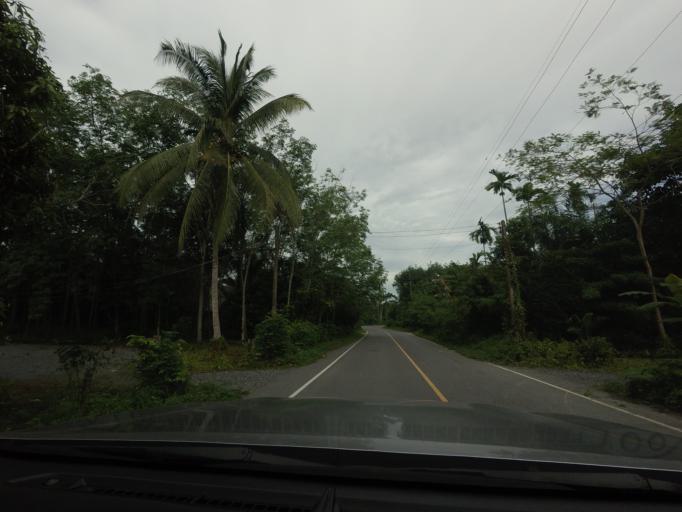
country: TH
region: Nakhon Si Thammarat
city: Phra Phrom
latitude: 8.2816
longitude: 99.9361
